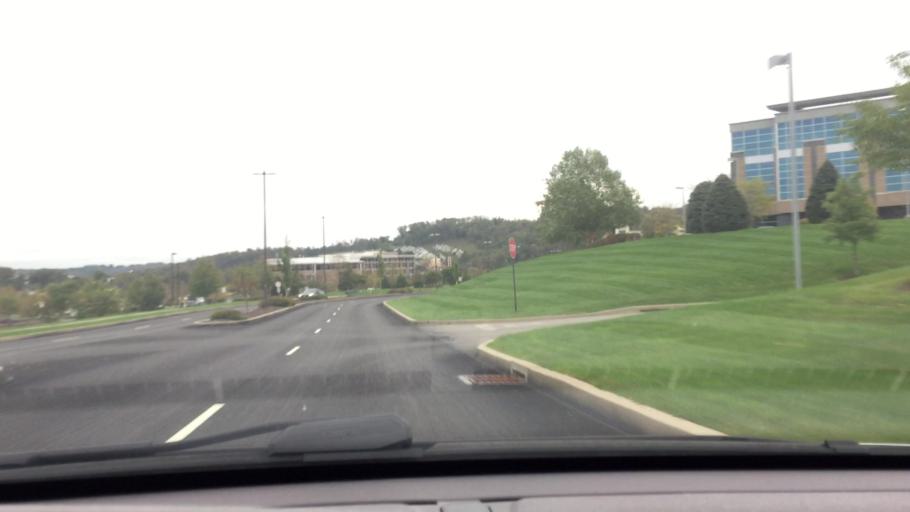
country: US
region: Pennsylvania
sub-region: Washington County
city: Canonsburg
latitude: 40.2786
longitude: -80.1685
